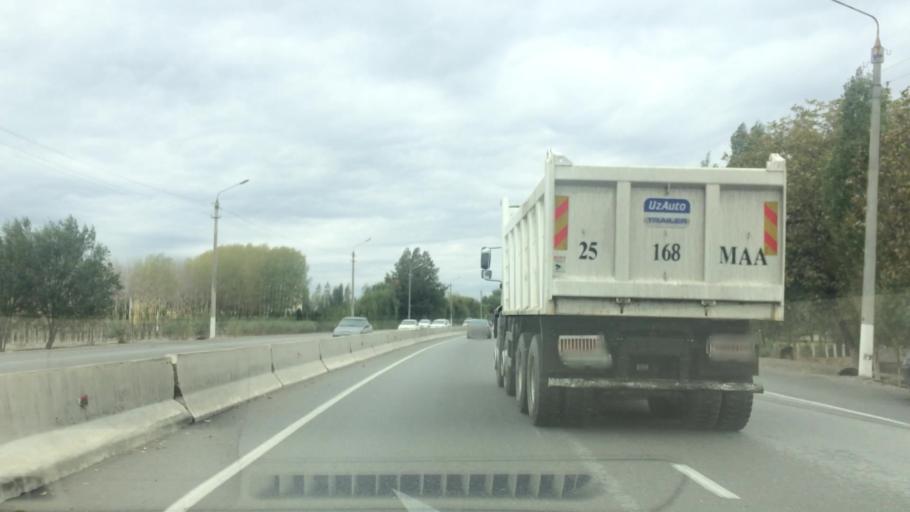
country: UZ
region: Jizzax
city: Jizzax
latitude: 39.9906
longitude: 67.5830
